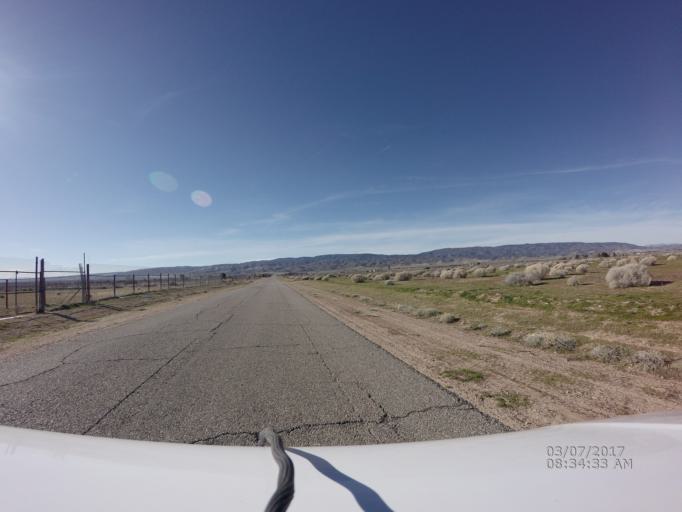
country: US
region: California
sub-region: Los Angeles County
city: Green Valley
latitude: 34.7970
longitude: -118.5369
